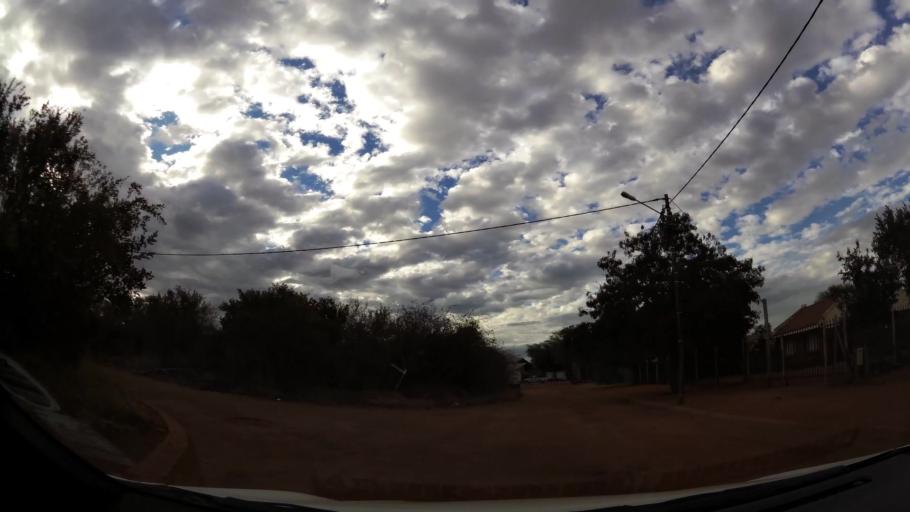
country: ZA
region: Limpopo
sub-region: Waterberg District Municipality
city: Modimolle
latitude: -24.5041
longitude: 28.7228
